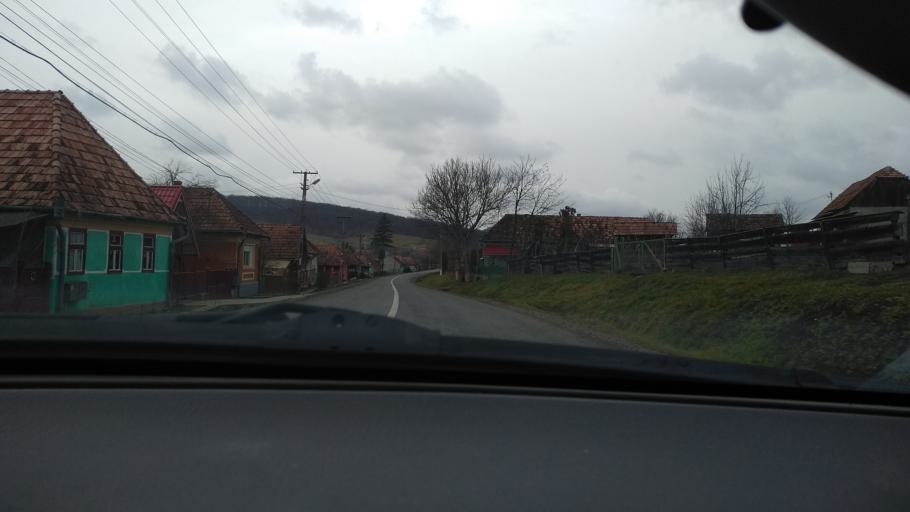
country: RO
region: Mures
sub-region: Comuna Galesti
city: Galesti
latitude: 46.5334
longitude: 24.7647
